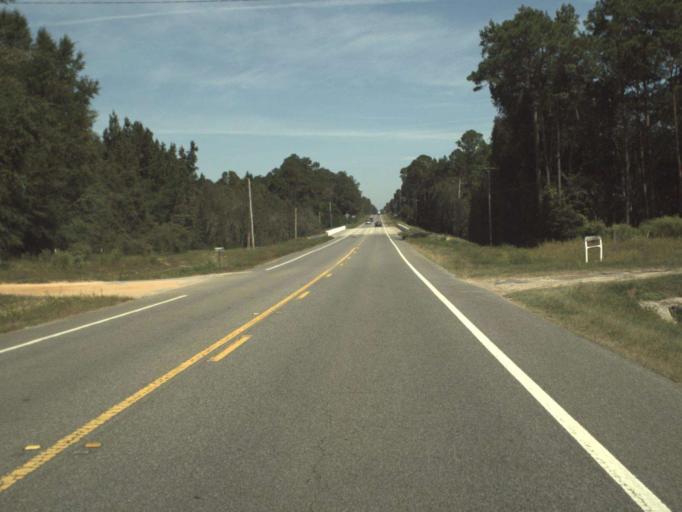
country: US
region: Florida
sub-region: Washington County
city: Chipley
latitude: 30.6614
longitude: -85.5777
